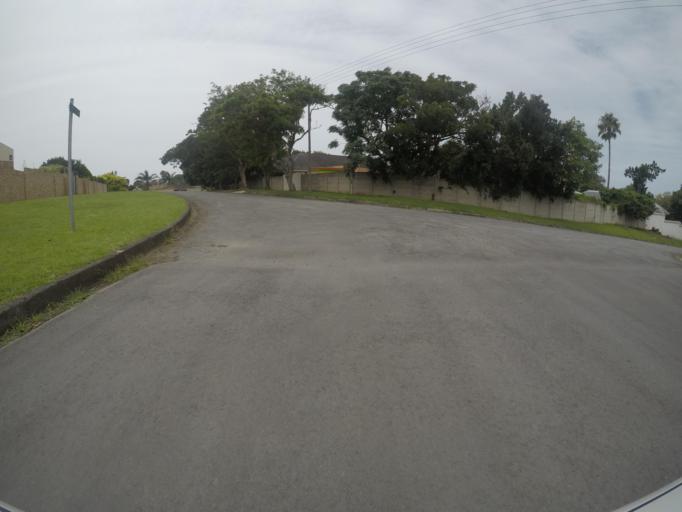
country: ZA
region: Eastern Cape
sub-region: Buffalo City Metropolitan Municipality
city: East London
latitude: -32.9650
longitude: 27.9303
